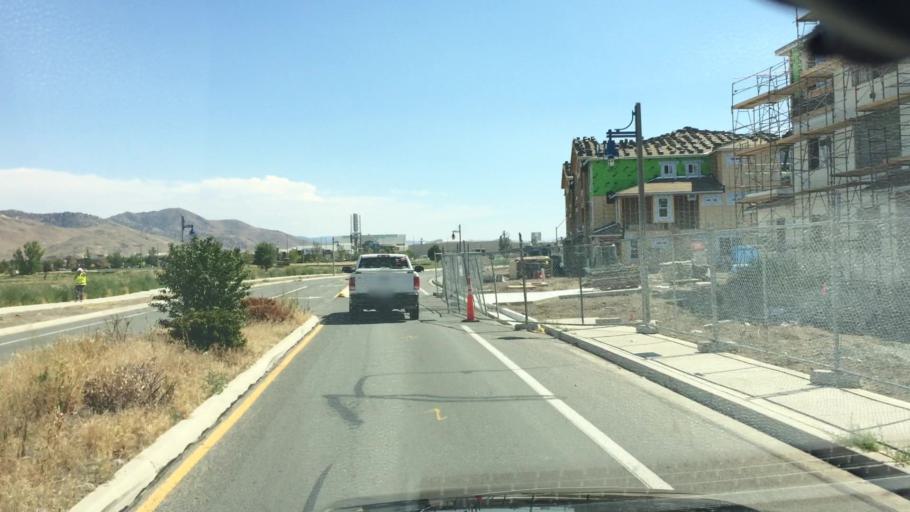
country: US
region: Nevada
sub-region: Washoe County
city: Sparks
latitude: 39.5388
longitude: -119.7219
